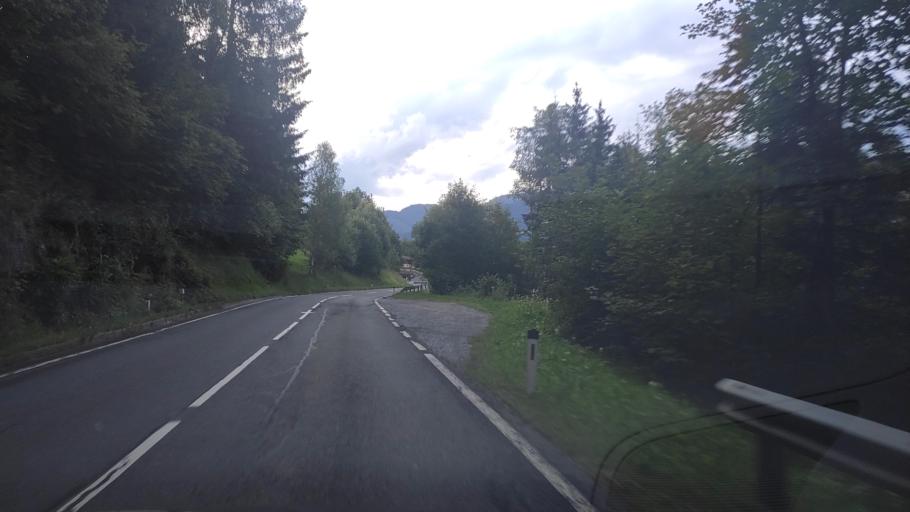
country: AT
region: Salzburg
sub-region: Politischer Bezirk Zell am See
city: Taxenbach
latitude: 47.2802
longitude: 12.9710
